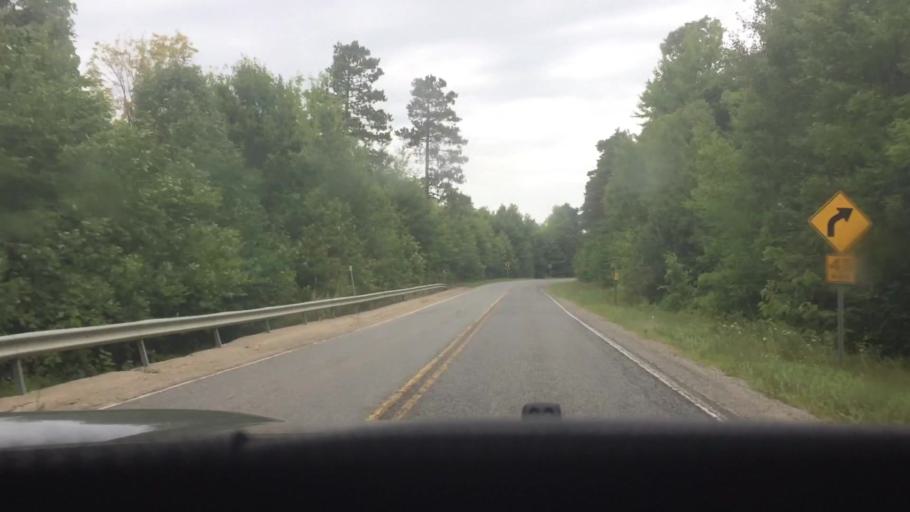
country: US
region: New York
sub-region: St. Lawrence County
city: Hannawa Falls
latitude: 44.6077
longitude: -74.8845
